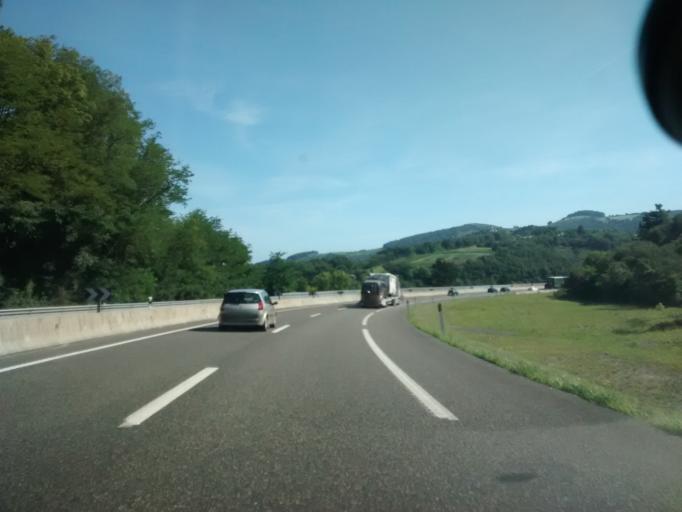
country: ES
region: Basque Country
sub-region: Provincia de Guipuzcoa
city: Zumaia
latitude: 43.2761
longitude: -2.2549
